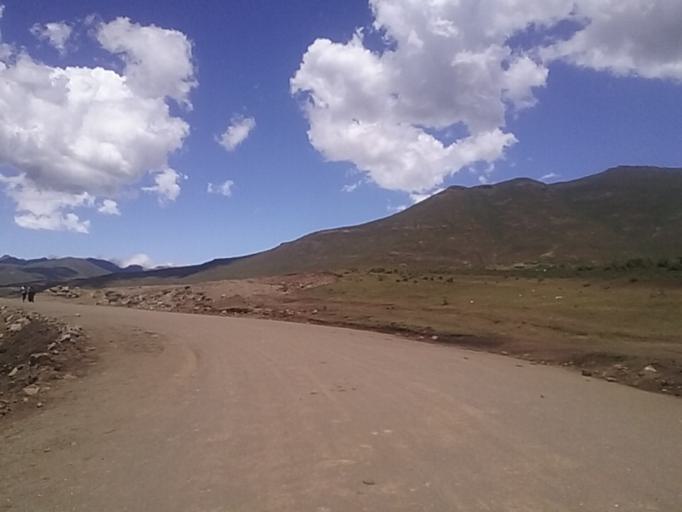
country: LS
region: Qacha's Nek
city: Qacha's Nek
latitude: -30.1690
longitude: 28.2106
